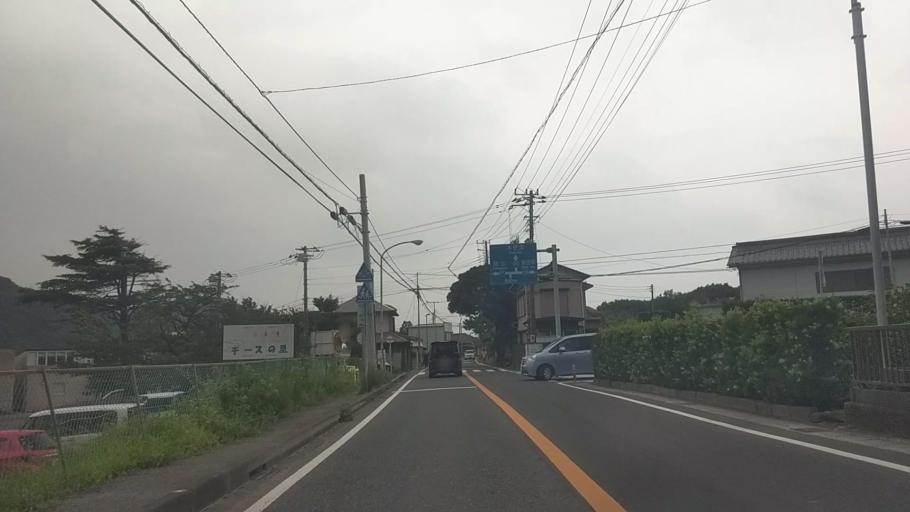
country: JP
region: Chiba
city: Tateyama
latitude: 35.1414
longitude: 139.8426
